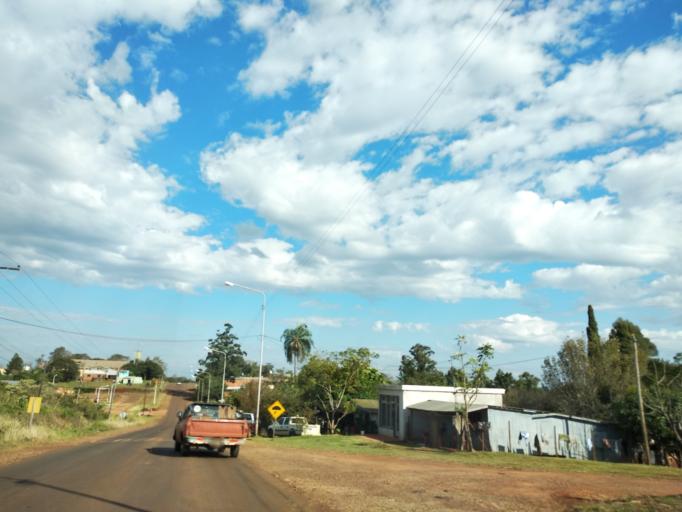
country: AR
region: Misiones
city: Aristobulo del Valle
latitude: -27.0807
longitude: -54.8314
